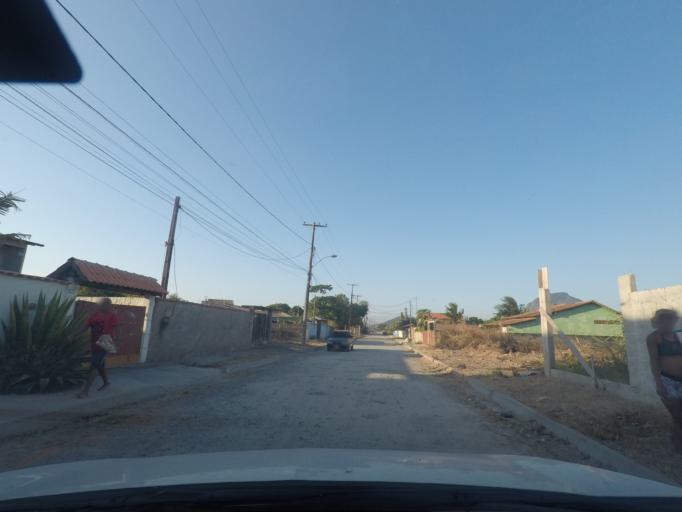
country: BR
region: Rio de Janeiro
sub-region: Marica
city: Marica
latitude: -22.9655
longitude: -42.9316
